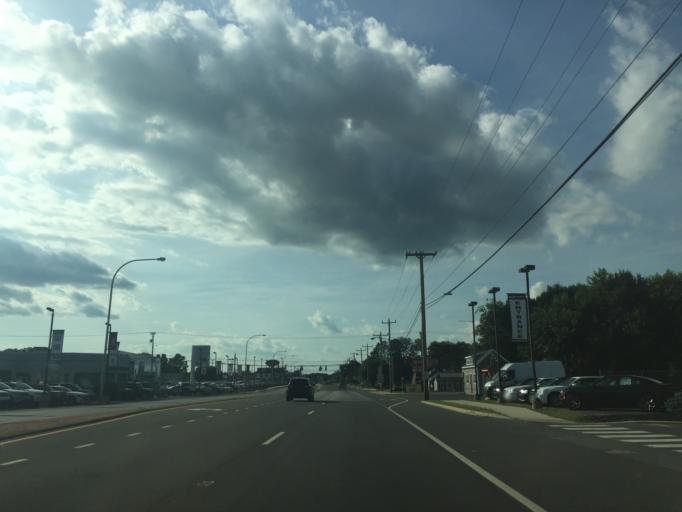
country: US
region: Delaware
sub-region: Kent County
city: Smyrna
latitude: 39.3015
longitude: -75.6028
